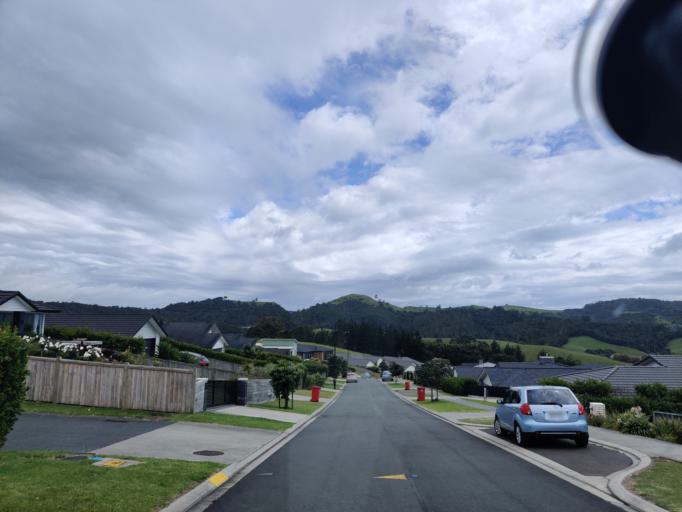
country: NZ
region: Auckland
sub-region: Auckland
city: Rothesay Bay
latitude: -36.5699
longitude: 174.6848
